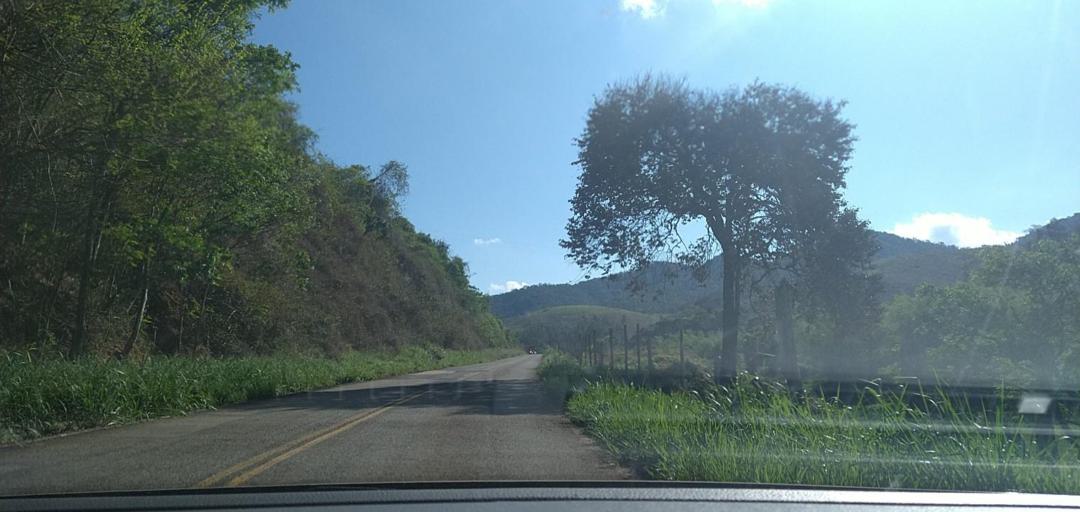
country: BR
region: Minas Gerais
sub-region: Alvinopolis
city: Alvinopolis
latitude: -20.1835
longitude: -42.9332
